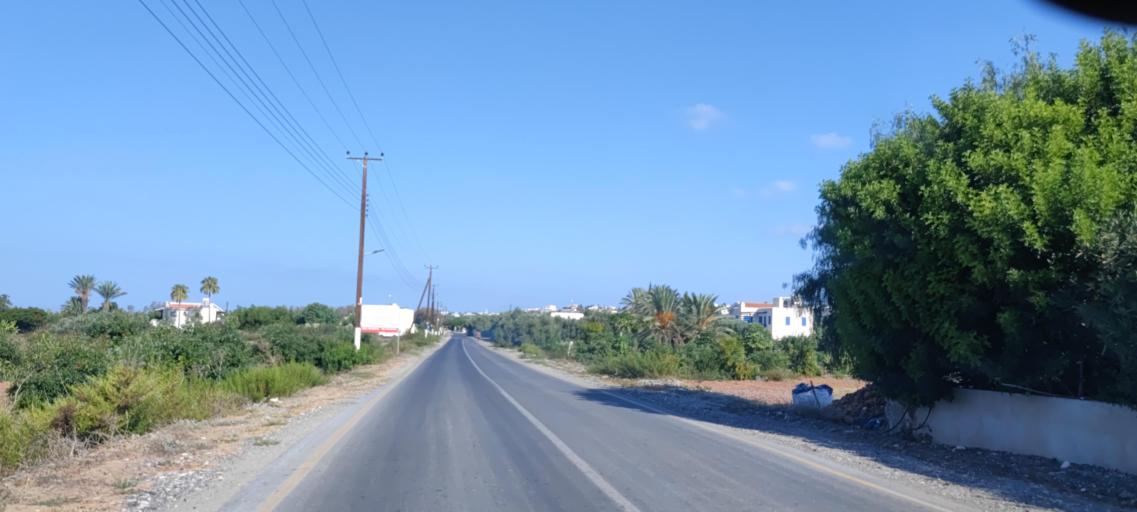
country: CY
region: Pafos
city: Pegeia
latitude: 34.8737
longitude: 32.3456
